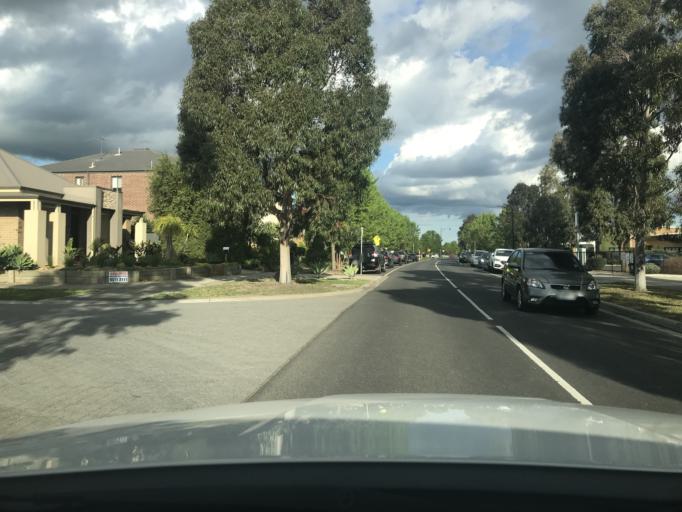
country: AU
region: Victoria
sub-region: Hume
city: Craigieburn
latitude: -37.5815
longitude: 144.9053
